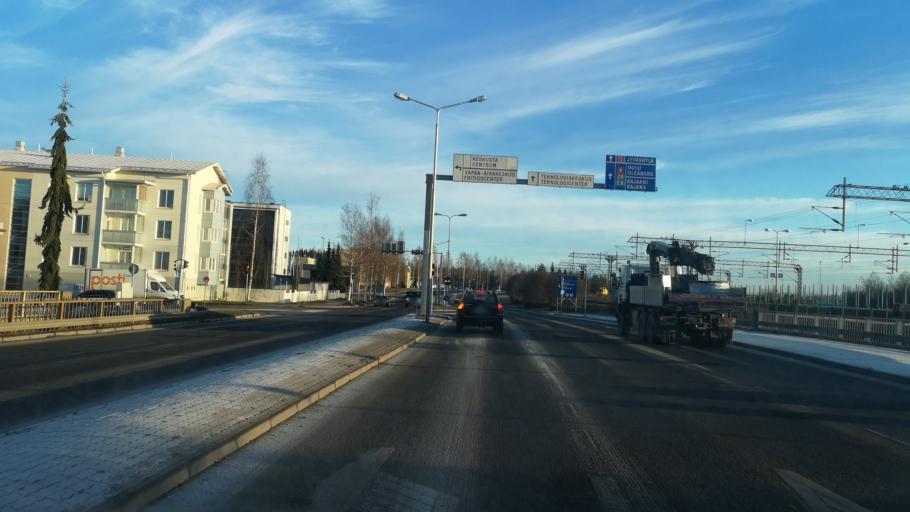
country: FI
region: Central Ostrobothnia
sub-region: Kokkola
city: Kokkola
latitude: 63.8352
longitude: 23.1376
